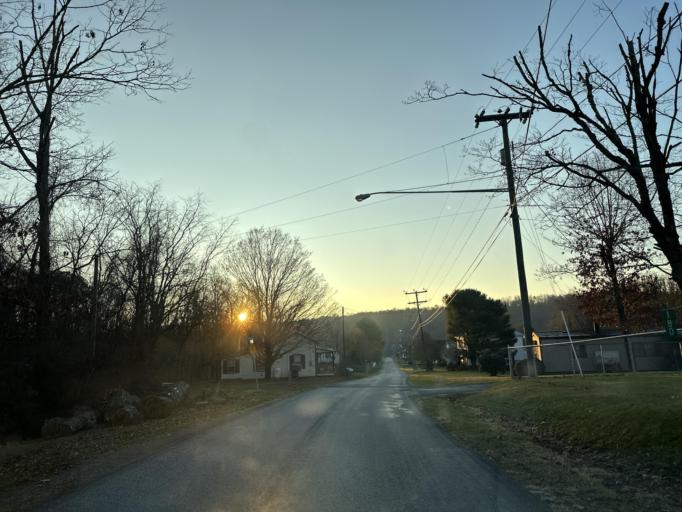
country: US
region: Virginia
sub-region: Rockbridge County
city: East Lexington
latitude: 38.0798
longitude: -79.3927
